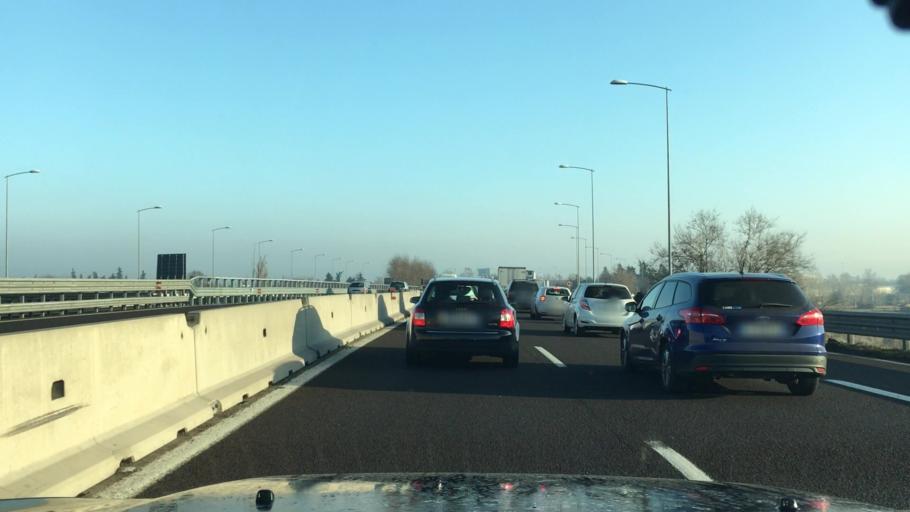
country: IT
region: Emilia-Romagna
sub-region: Provincia di Bologna
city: Calderara di Reno
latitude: 44.5205
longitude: 11.2849
